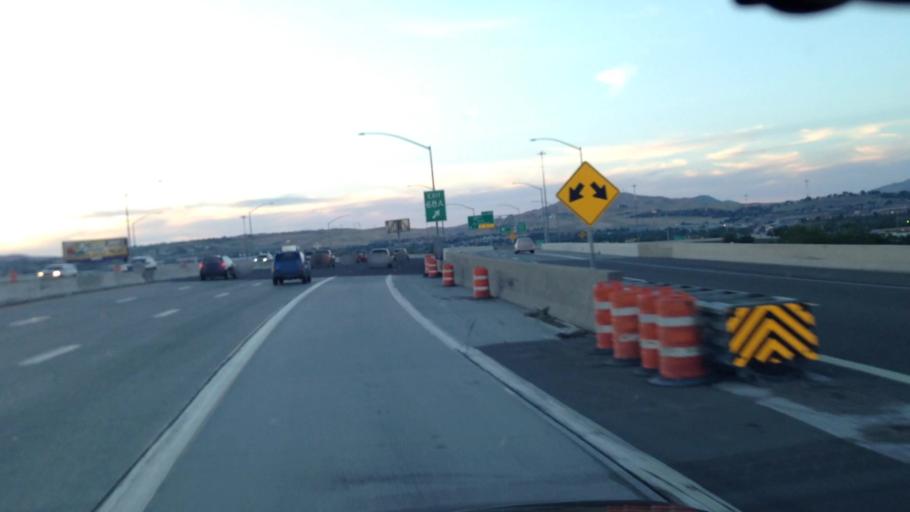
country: US
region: Nevada
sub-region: Washoe County
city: Reno
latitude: 39.5324
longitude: -119.7868
